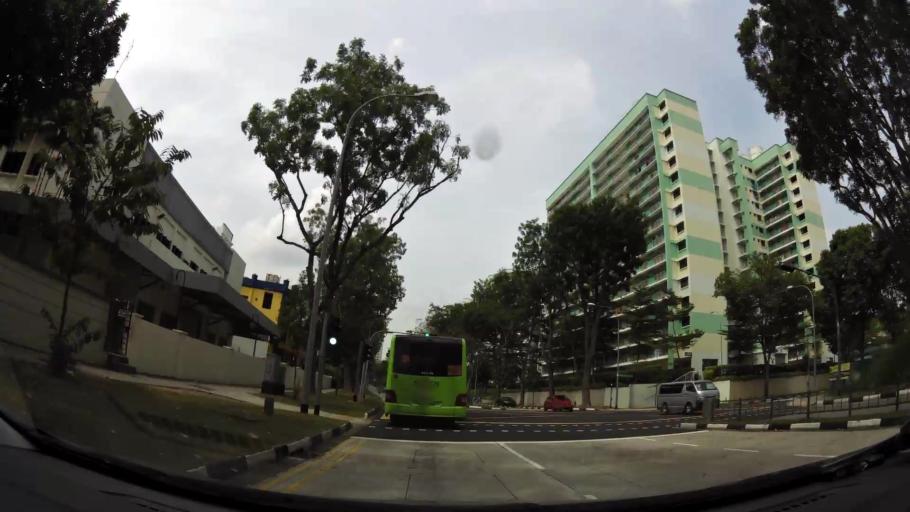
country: SG
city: Singapore
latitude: 1.3450
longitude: 103.7514
